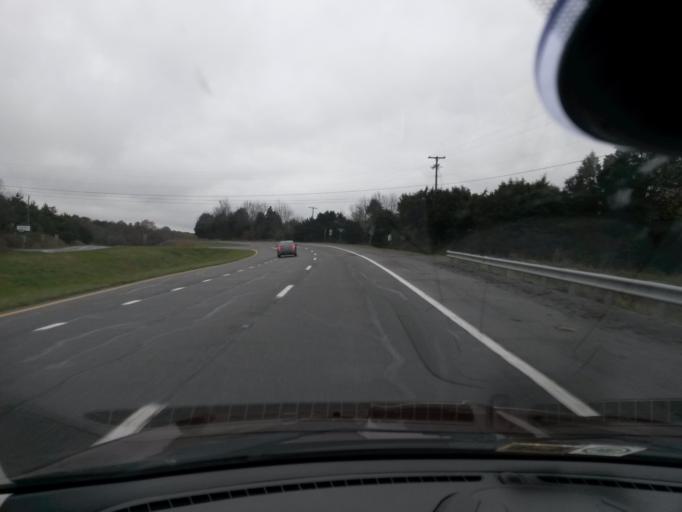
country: US
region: Virginia
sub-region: Botetourt County
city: Fincastle
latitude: 37.5191
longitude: -79.8786
